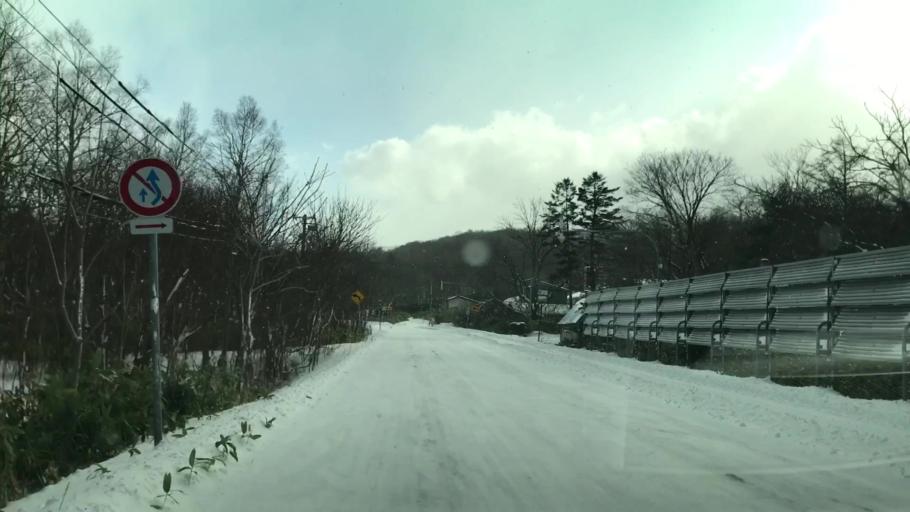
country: JP
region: Hokkaido
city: Yoichi
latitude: 43.3324
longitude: 140.4677
